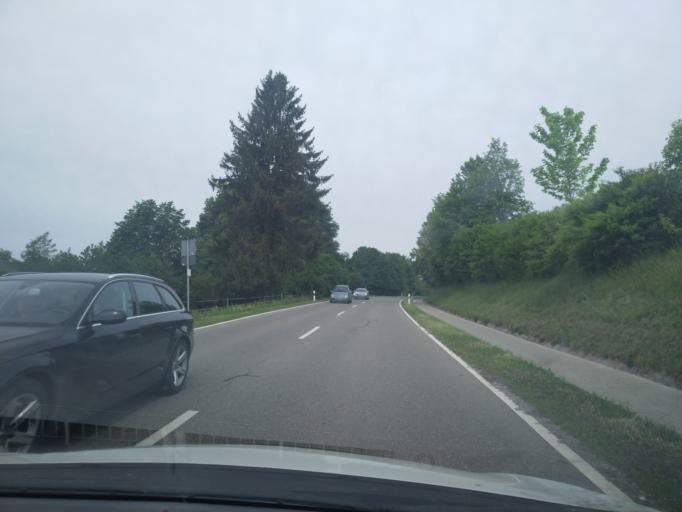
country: DE
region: Baden-Wuerttemberg
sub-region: Freiburg Region
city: Bonndorf im Schwarzwald
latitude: 47.8112
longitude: 8.3454
